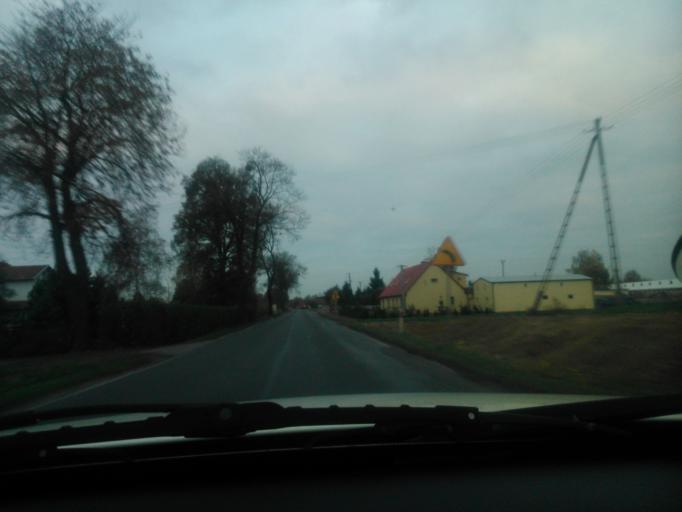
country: PL
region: Kujawsko-Pomorskie
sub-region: Powiat golubsko-dobrzynski
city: Golub-Dobrzyn
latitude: 53.1344
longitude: 19.0112
